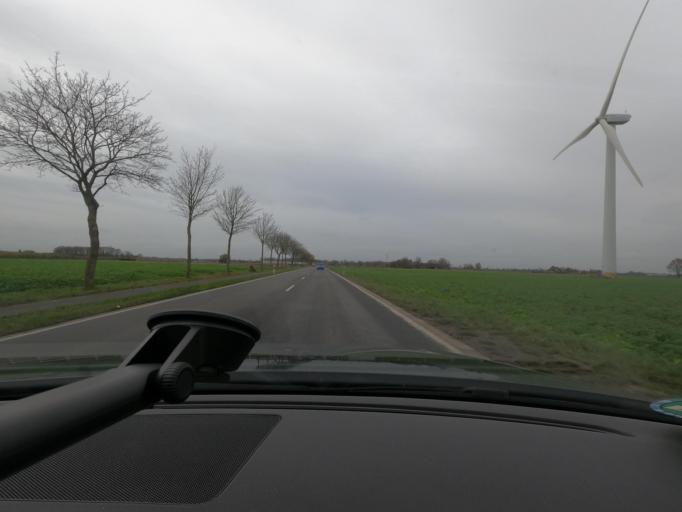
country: DE
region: North Rhine-Westphalia
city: Tonisvorst
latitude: 51.3456
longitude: 6.4804
